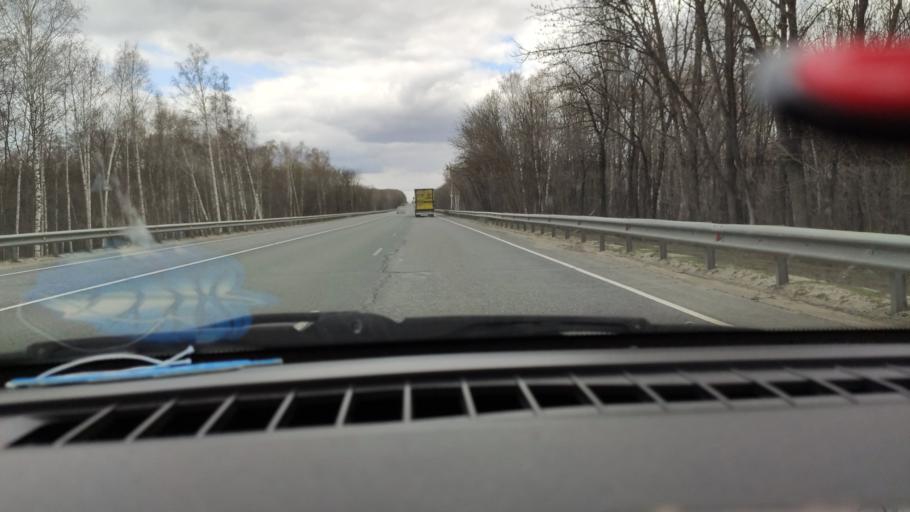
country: RU
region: Saratov
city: Vol'sk
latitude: 52.1066
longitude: 47.4214
